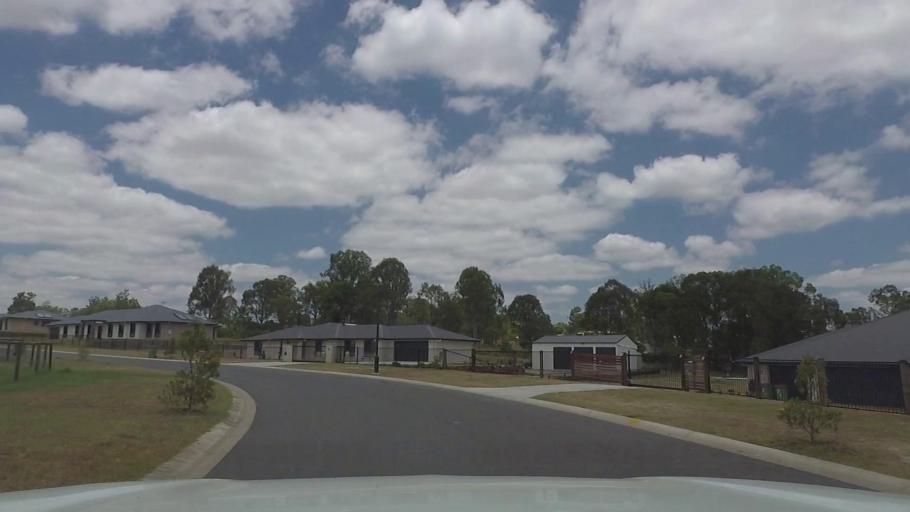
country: AU
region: Queensland
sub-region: Ipswich
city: Springfield Lakes
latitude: -27.7346
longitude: 152.9485
